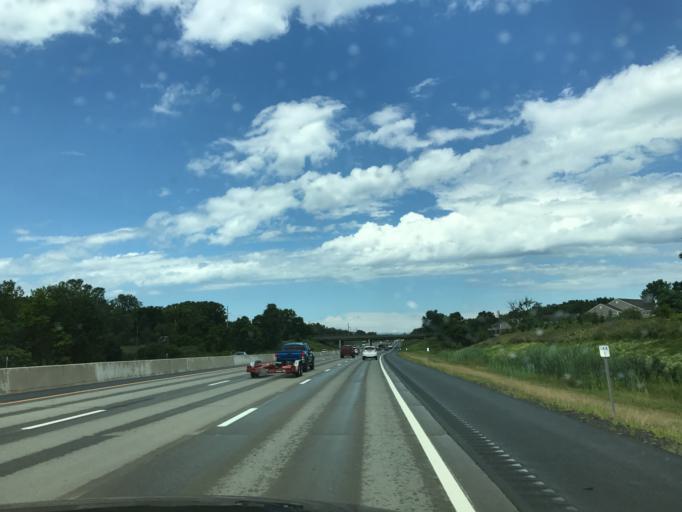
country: US
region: New York
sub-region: Albany County
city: Delmar
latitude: 42.6510
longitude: -73.8154
